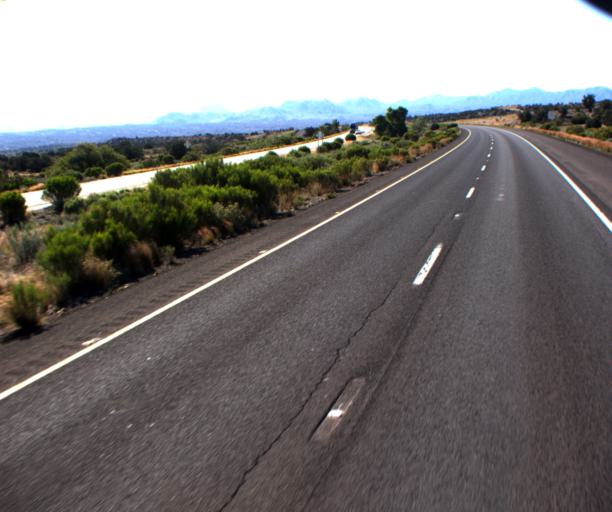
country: US
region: Arizona
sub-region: Mohave County
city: New Kingman-Butler
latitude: 35.1477
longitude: -113.6883
